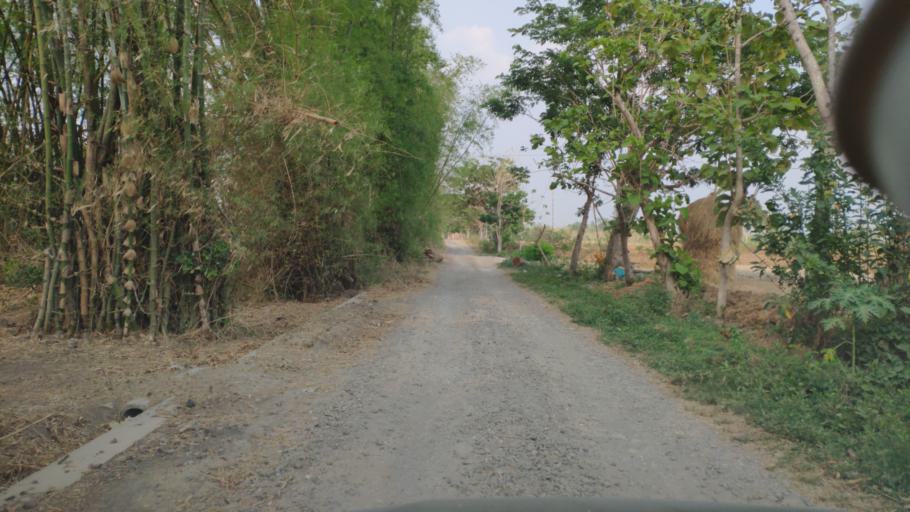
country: ID
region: Central Java
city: Pipes
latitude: -7.0583
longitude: 111.2765
